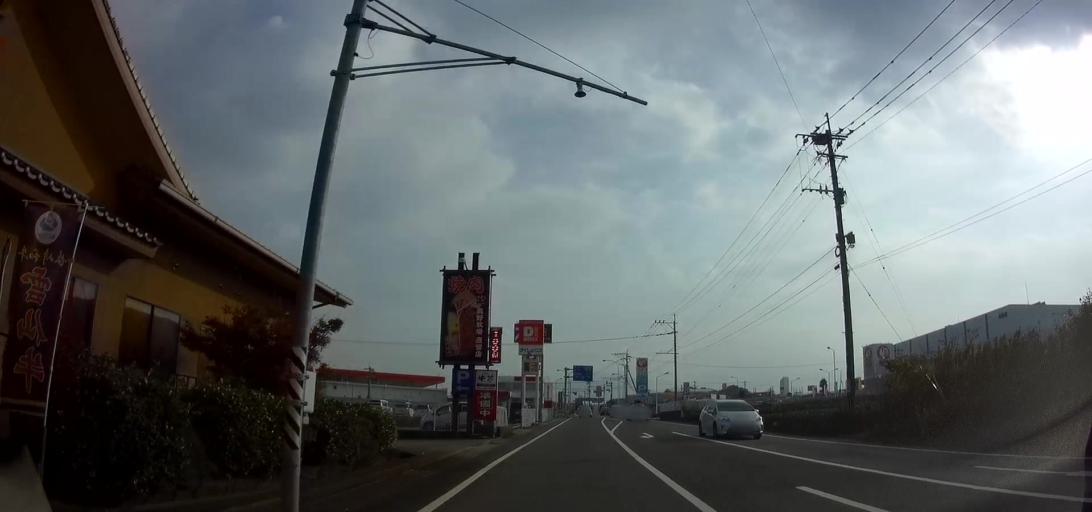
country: JP
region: Nagasaki
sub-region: Isahaya-shi
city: Isahaya
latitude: 32.7962
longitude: 130.1633
